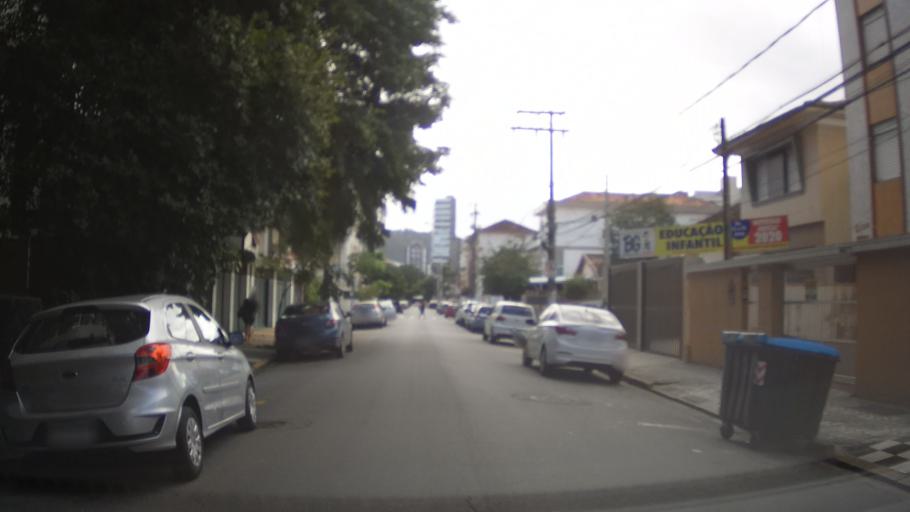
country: BR
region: Sao Paulo
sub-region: Santos
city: Santos
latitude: -23.9541
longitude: -46.3341
